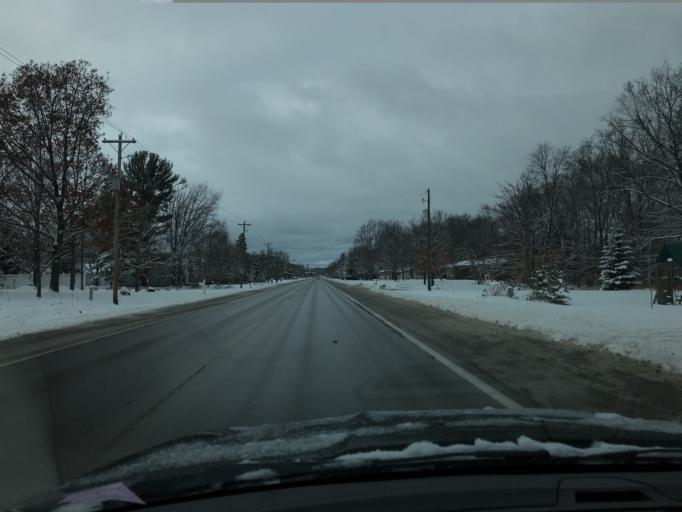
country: US
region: Michigan
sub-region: Charlevoix County
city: Charlevoix
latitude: 45.2891
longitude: -85.2462
